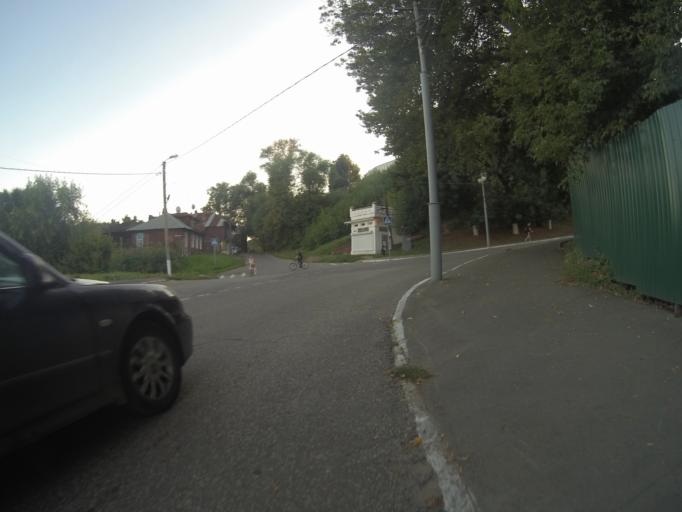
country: RU
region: Vladimir
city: Vladimir
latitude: 56.1311
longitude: 40.4170
